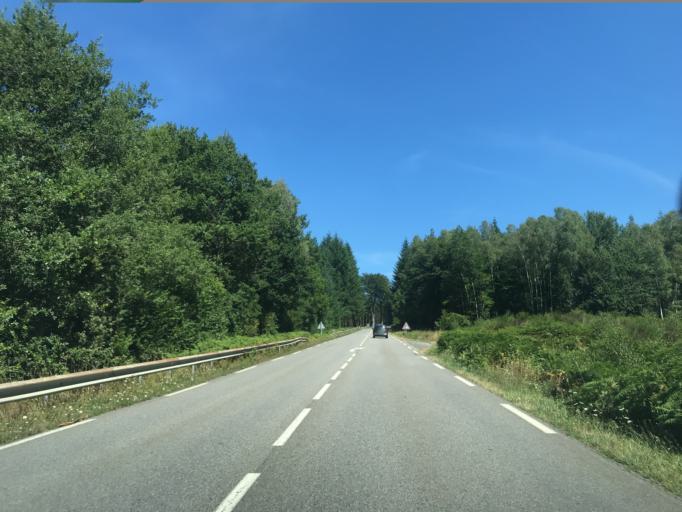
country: FR
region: Limousin
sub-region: Departement de la Correze
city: Egletons
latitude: 45.4547
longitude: 2.1136
